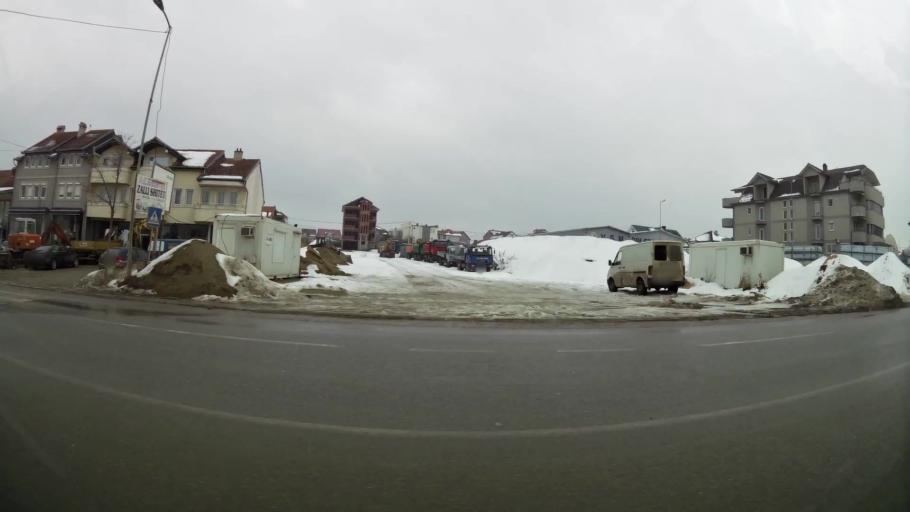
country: XK
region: Pristina
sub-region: Komuna e Prishtines
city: Pristina
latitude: 42.6991
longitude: 21.1593
